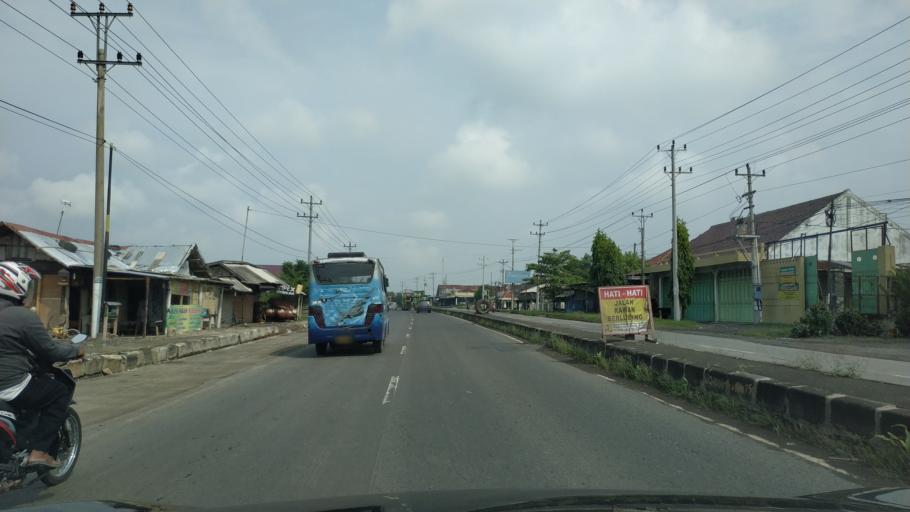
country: ID
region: Central Java
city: Bulakamba
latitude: -6.8714
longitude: 108.8977
